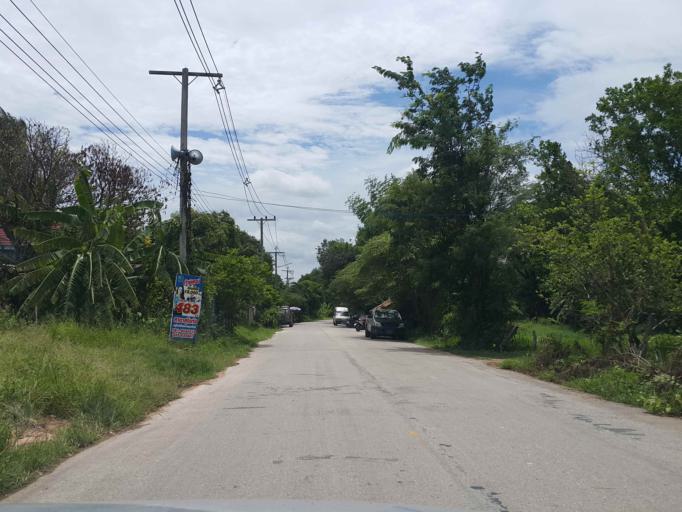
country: TH
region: Sukhothai
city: Ban Na
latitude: 17.0093
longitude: 99.7062
